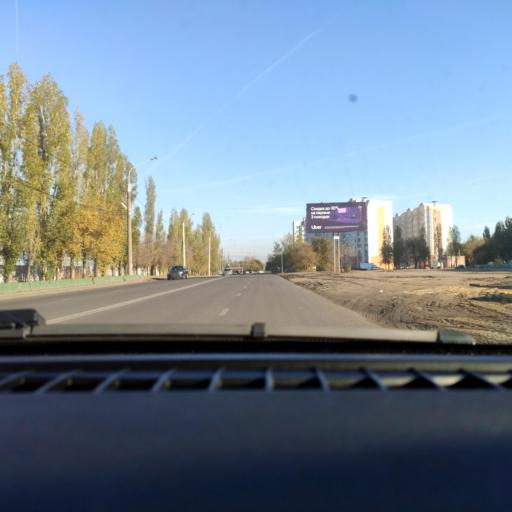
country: RU
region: Voronezj
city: Voronezh
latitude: 51.6424
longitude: 39.2664
